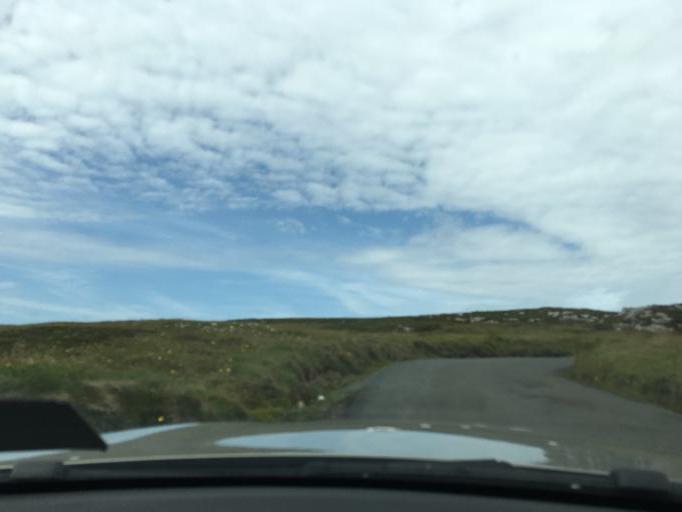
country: IE
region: Ulster
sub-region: County Donegal
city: Carndonagh
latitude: 55.3790
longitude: -7.3744
